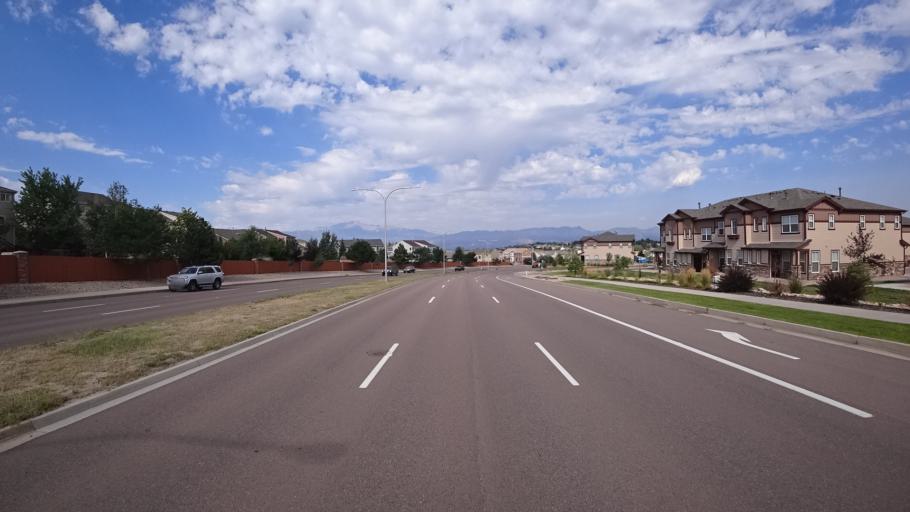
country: US
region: Colorado
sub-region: El Paso County
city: Cimarron Hills
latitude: 38.9118
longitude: -104.7293
